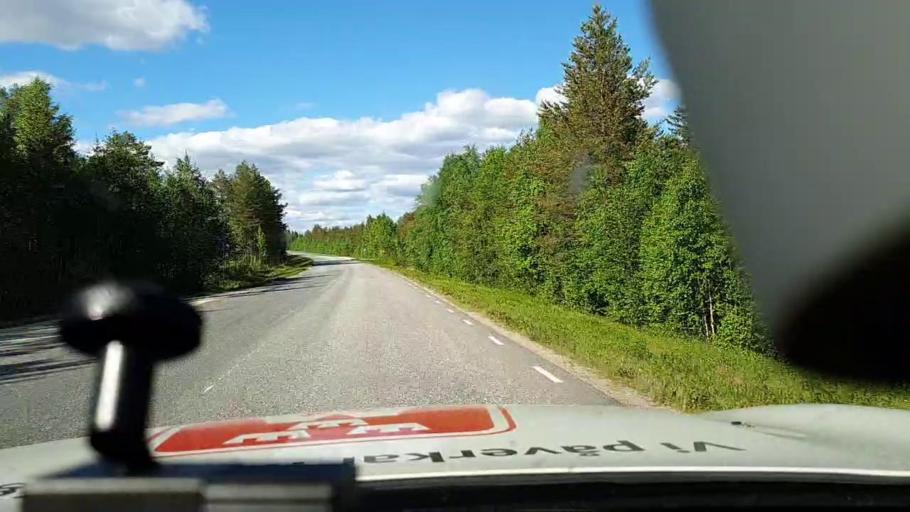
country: FI
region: Lapland
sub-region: Torniolaakso
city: Ylitornio
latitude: 66.3408
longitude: 23.6466
